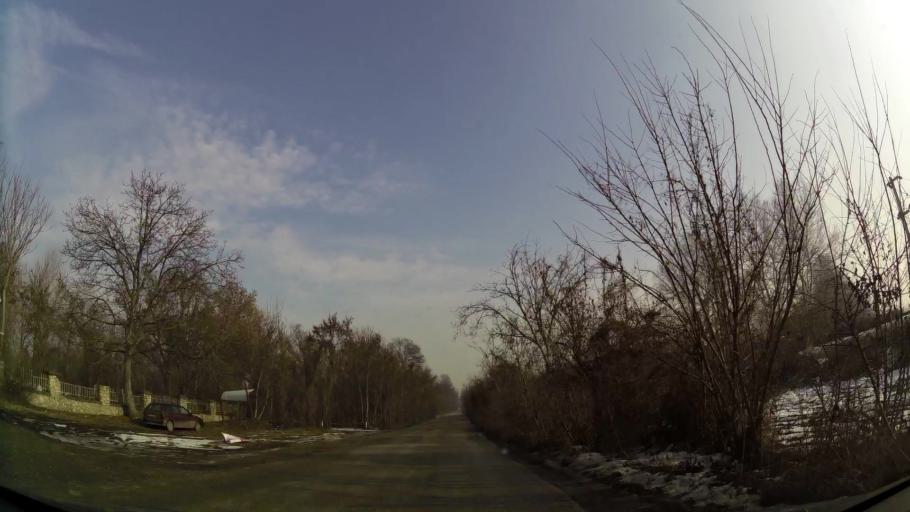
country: MK
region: Ilinden
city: Jurumleri
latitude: 41.9913
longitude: 21.5232
